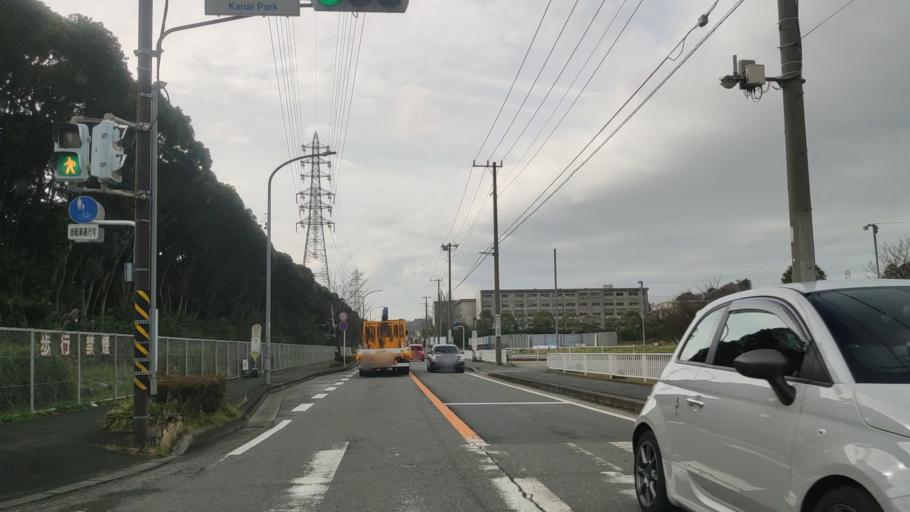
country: JP
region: Kanagawa
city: Fujisawa
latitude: 35.3767
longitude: 139.5252
